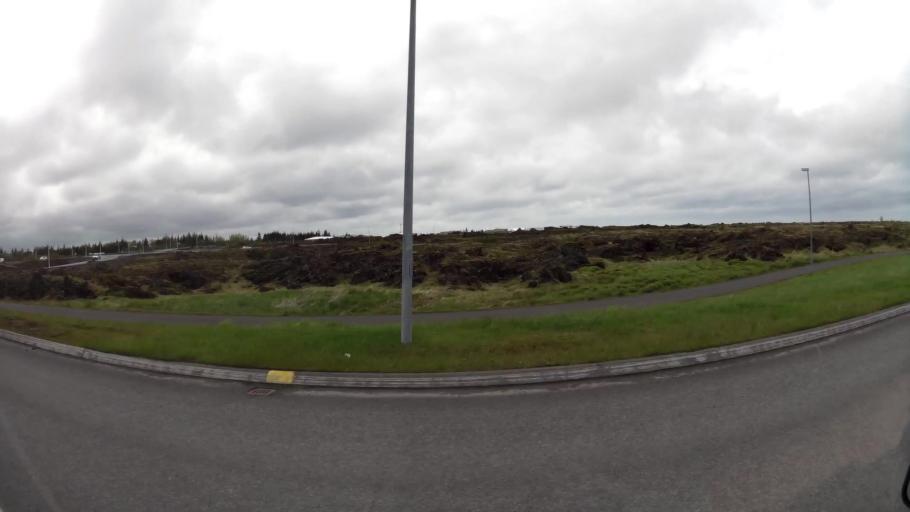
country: IS
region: Capital Region
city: Hafnarfjoerdur
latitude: 64.0868
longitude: -21.9514
